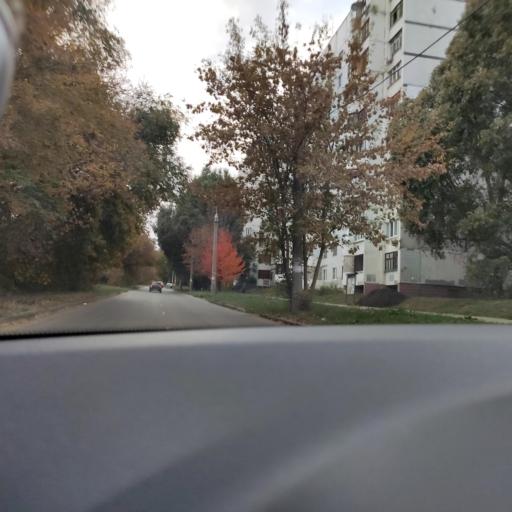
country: RU
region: Samara
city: Petra-Dubrava
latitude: 53.2494
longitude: 50.2642
